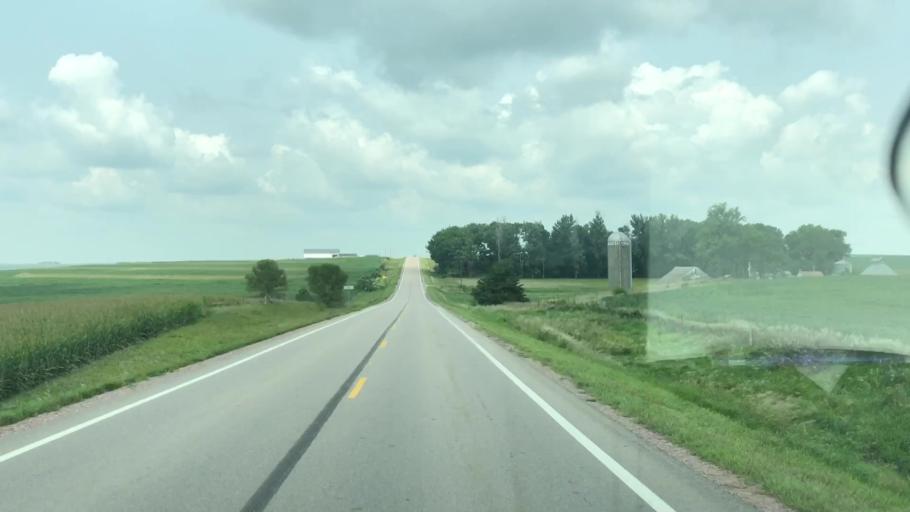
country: US
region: Iowa
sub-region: Plymouth County
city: Kingsley
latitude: 42.5964
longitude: -95.9572
